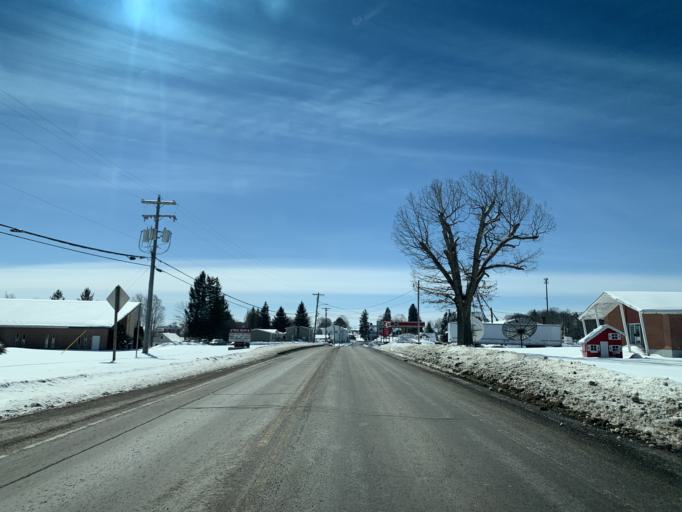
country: US
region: Pennsylvania
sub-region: Somerset County
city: Meyersdale
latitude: 39.7015
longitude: -79.1615
